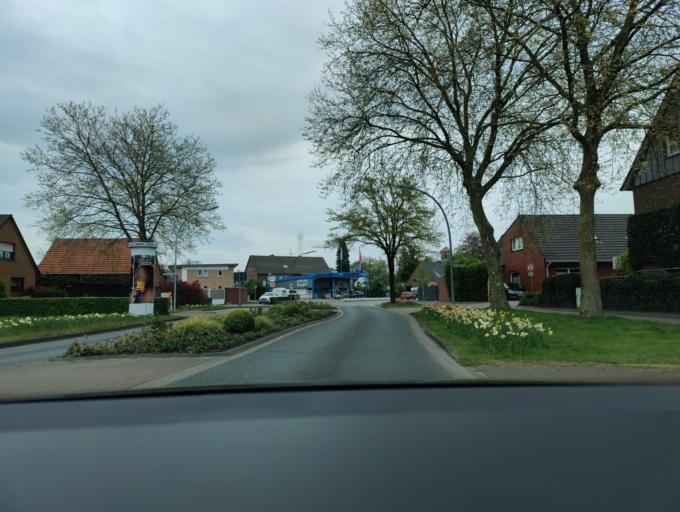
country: DE
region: Lower Saxony
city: Lingen
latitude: 52.5303
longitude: 7.3112
